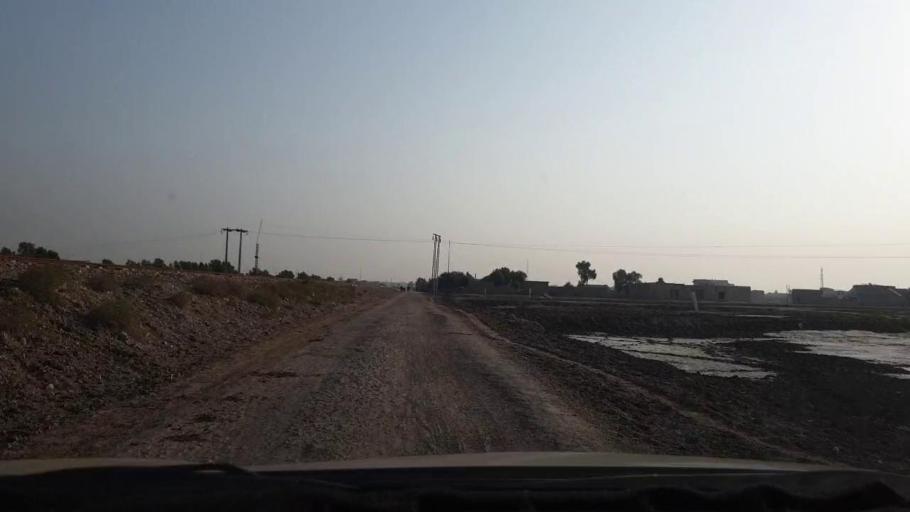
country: PK
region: Sindh
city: Larkana
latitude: 27.5274
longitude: 68.1973
